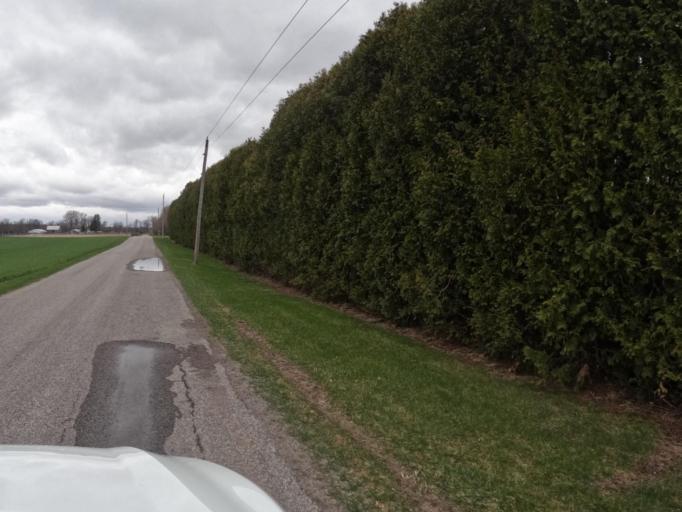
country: CA
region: Ontario
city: Norfolk County
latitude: 42.9596
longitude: -80.4265
